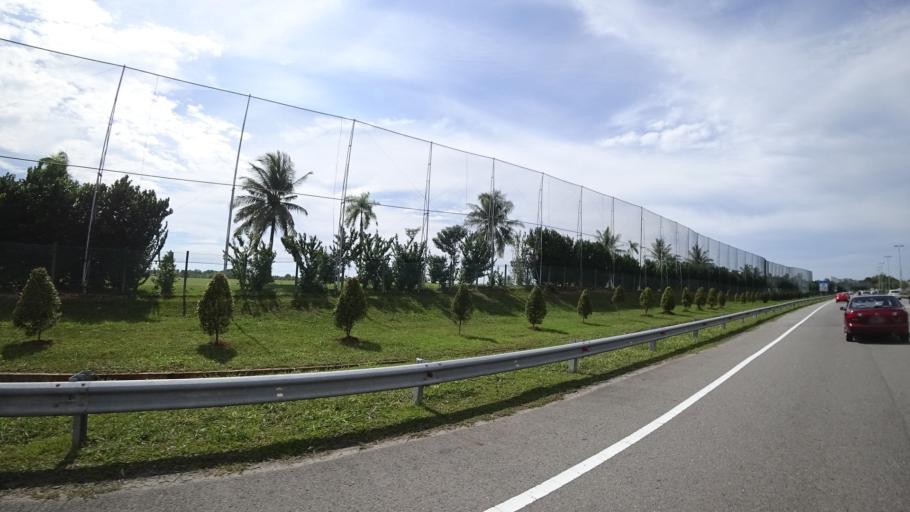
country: BN
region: Brunei and Muara
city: Bandar Seri Begawan
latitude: 4.9303
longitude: 114.9248
